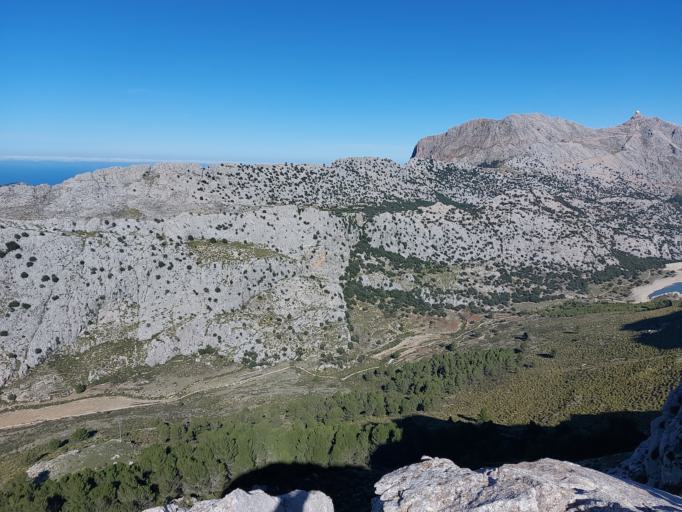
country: ES
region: Balearic Islands
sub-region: Illes Balears
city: Fornalutx
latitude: 39.7689
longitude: 2.7760
